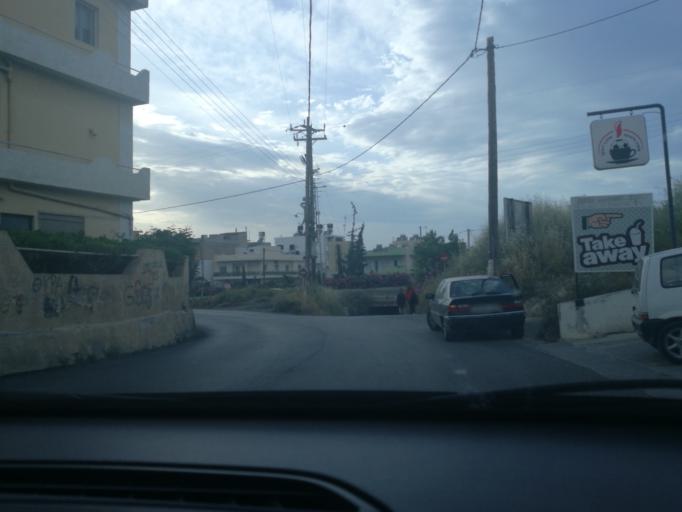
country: GR
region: Crete
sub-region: Nomos Irakleiou
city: Irakleion
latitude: 35.3180
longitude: 25.1355
